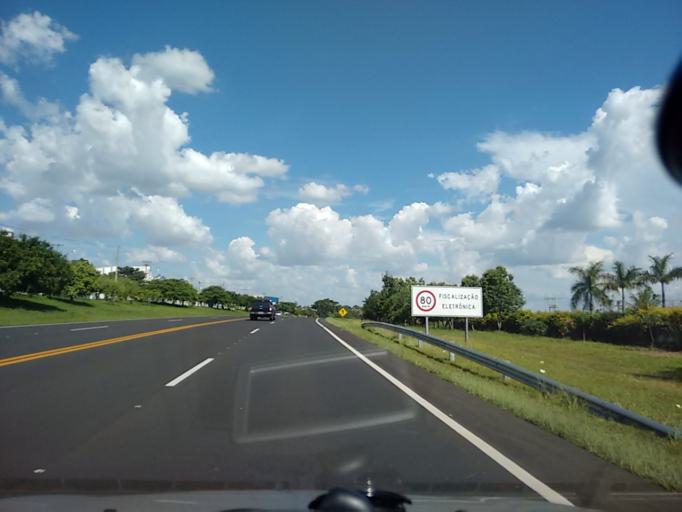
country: BR
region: Sao Paulo
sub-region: Pompeia
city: Pompeia
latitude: -22.1459
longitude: -50.1015
